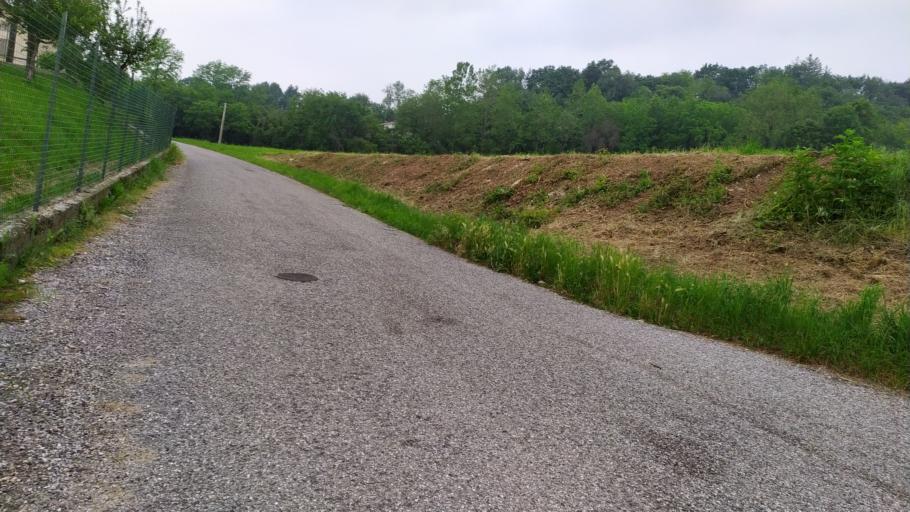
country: IT
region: Friuli Venezia Giulia
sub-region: Provincia di Udine
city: Majano
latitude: 46.1875
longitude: 13.0510
